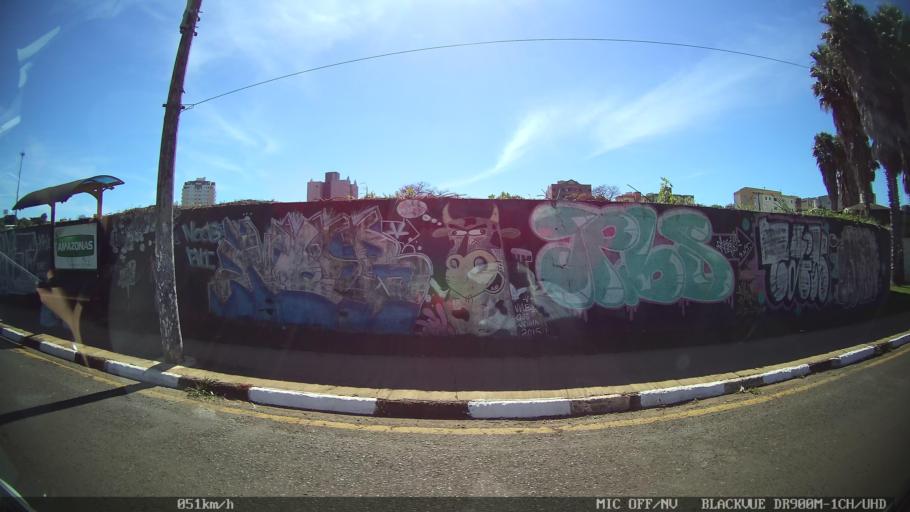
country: BR
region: Sao Paulo
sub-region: Franca
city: Franca
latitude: -20.5522
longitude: -47.4082
